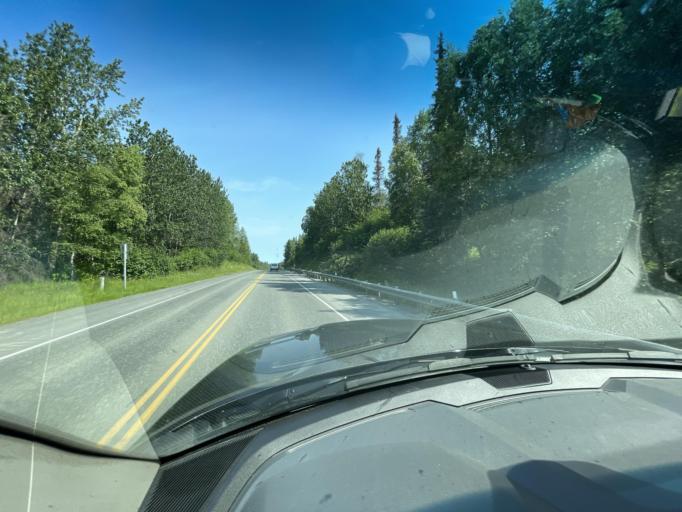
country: US
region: Alaska
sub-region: Kenai Peninsula Borough
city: Soldotna
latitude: 60.4583
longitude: -151.0969
